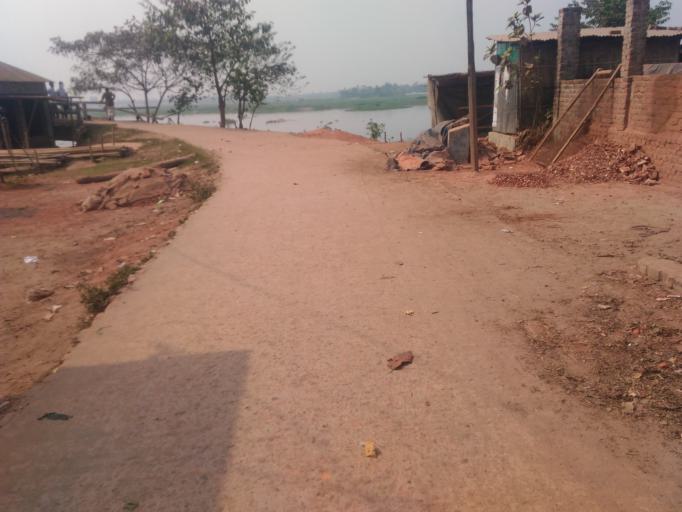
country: BD
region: Dhaka
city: Narayanganj
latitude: 23.6387
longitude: 90.4347
